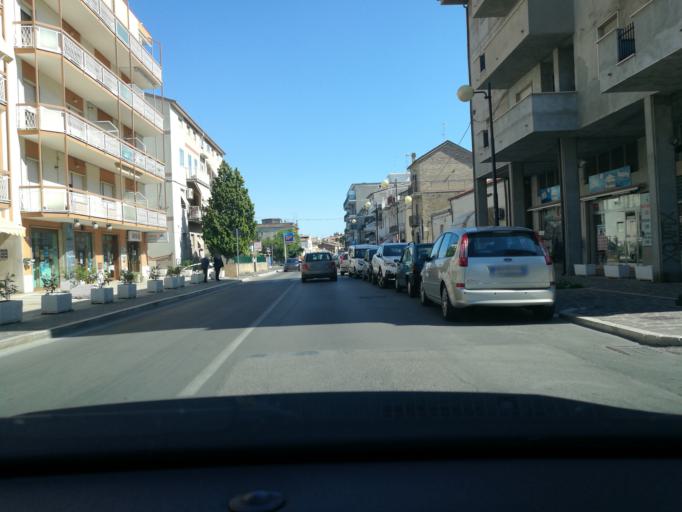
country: IT
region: Abruzzo
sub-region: Provincia di Chieti
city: Vasto
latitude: 42.1190
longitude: 14.7078
